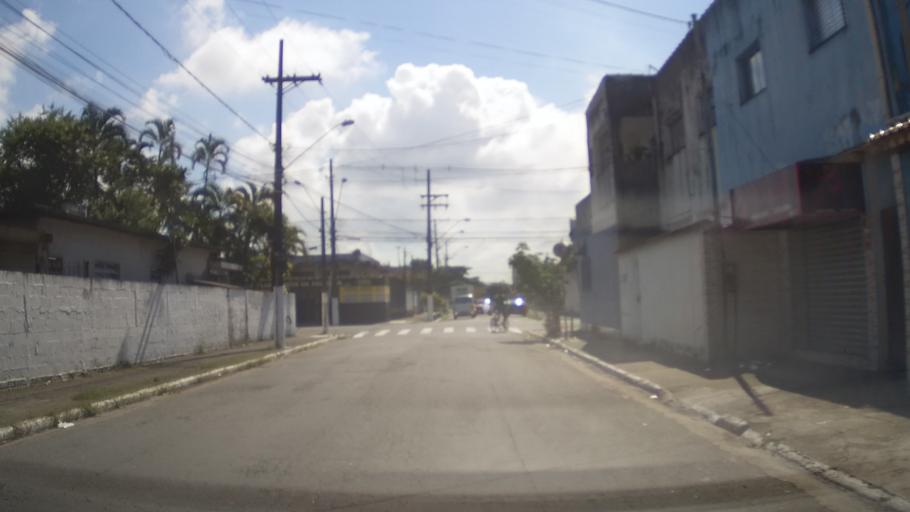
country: BR
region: Sao Paulo
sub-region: Praia Grande
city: Praia Grande
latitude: -24.0183
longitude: -46.4775
